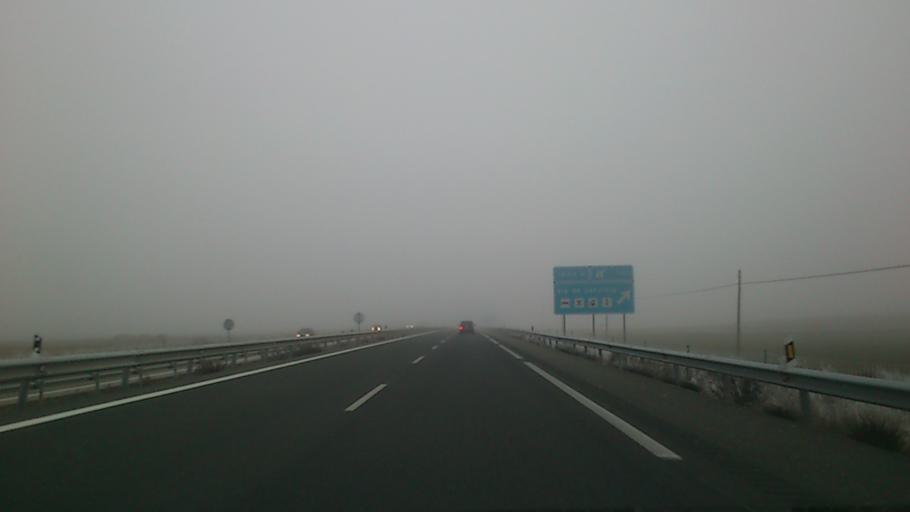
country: ES
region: Castille-La Mancha
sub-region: Provincia de Guadalajara
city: Almadrones
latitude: 40.8861
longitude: -2.7807
